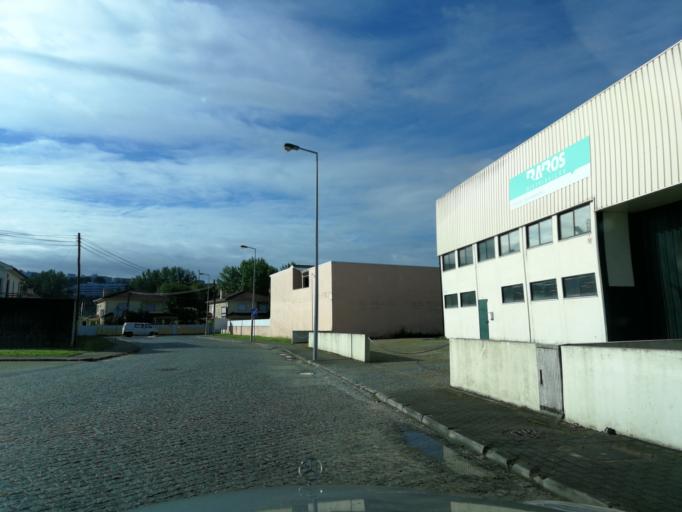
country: PT
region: Braga
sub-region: Braga
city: Braga
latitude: 41.5627
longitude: -8.4445
